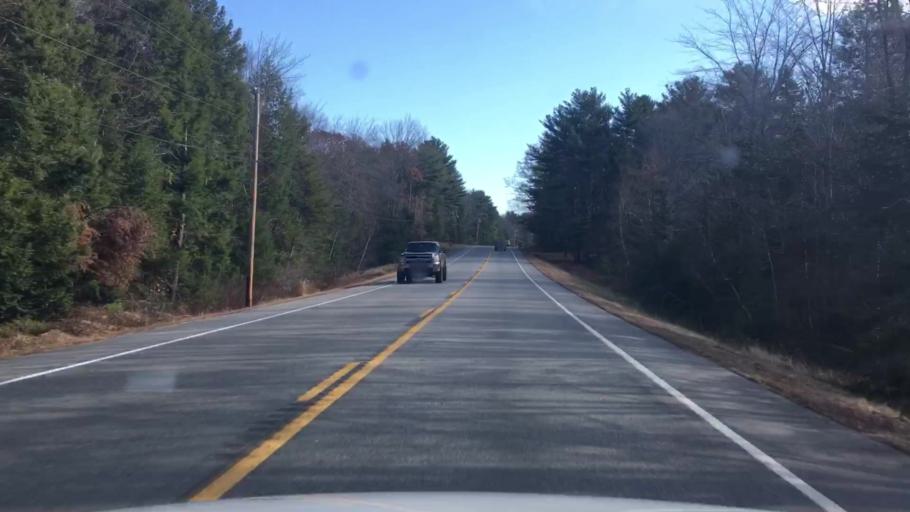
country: US
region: Maine
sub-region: Lincoln County
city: Jefferson
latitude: 44.2593
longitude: -69.4520
